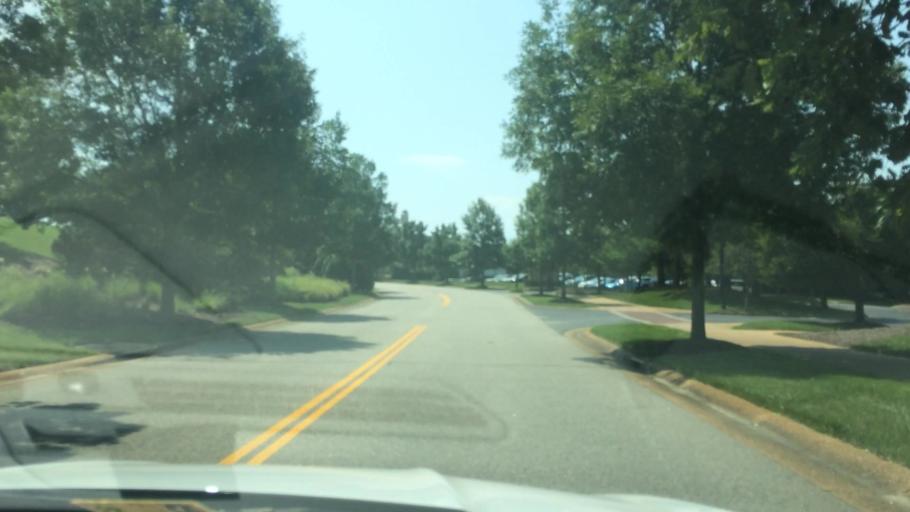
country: US
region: Virginia
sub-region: James City County
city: Williamsburg
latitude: 37.3524
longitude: -76.7695
